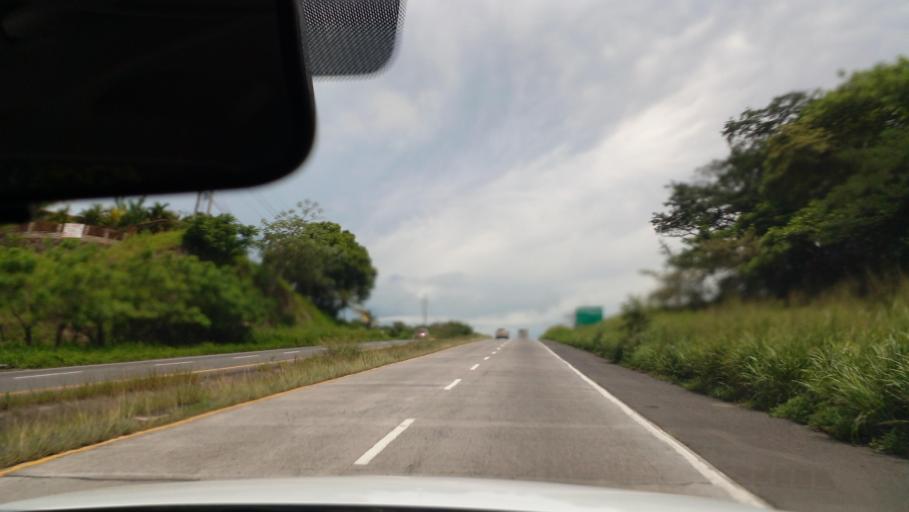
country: PA
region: Panama
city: Nueva Gorgona
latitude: 8.4910
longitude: -79.9581
